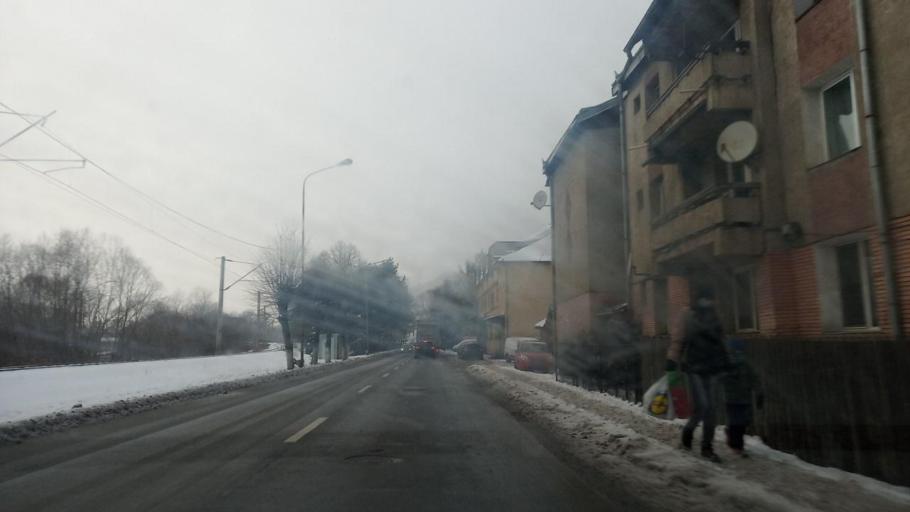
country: RO
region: Suceava
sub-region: Municipiul Vatra Dornei
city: Vatra Dornei
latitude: 47.3464
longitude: 25.3512
